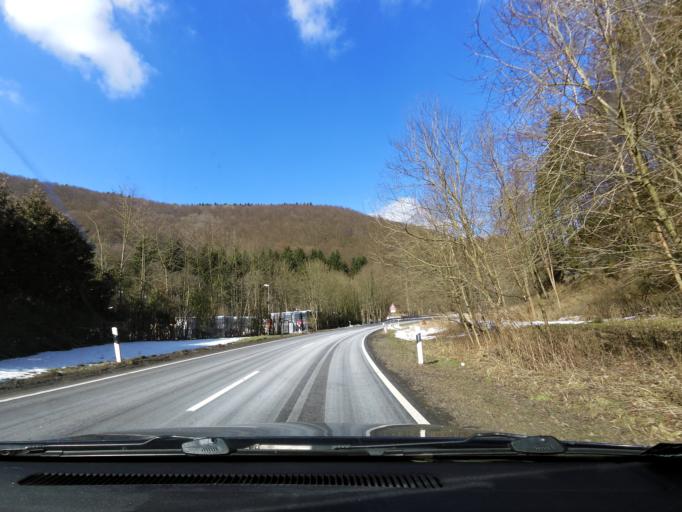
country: DE
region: Lower Saxony
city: Bad Lauterberg im Harz
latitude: 51.6498
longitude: 10.4849
